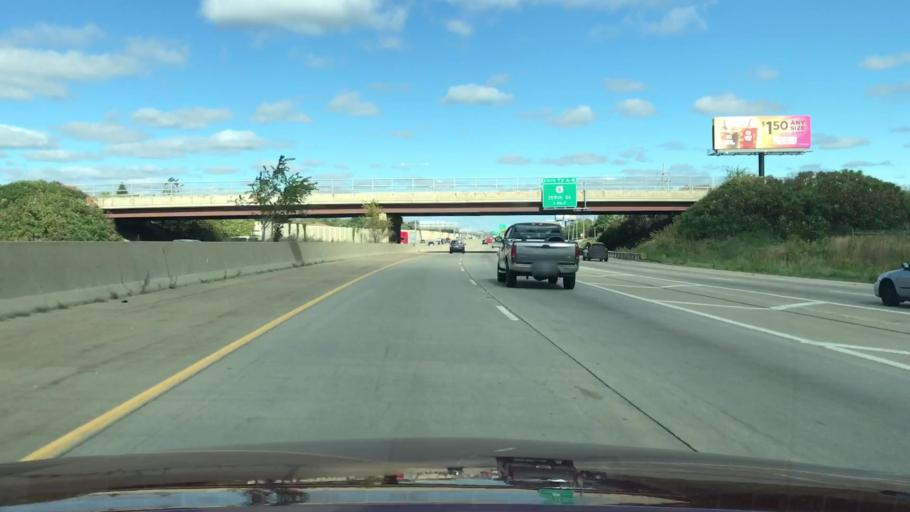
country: US
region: Illinois
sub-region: Cook County
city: South Holland
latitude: 41.5854
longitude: -87.5834
